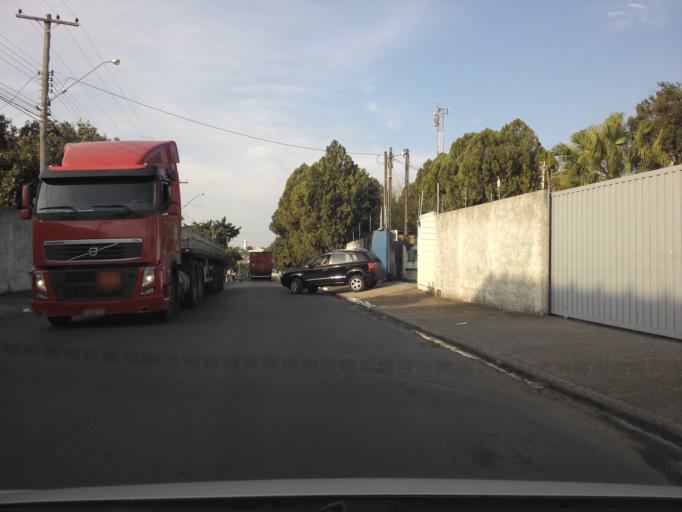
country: BR
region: Sao Paulo
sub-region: Hortolandia
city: Hortolandia
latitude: -22.9079
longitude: -47.2096
